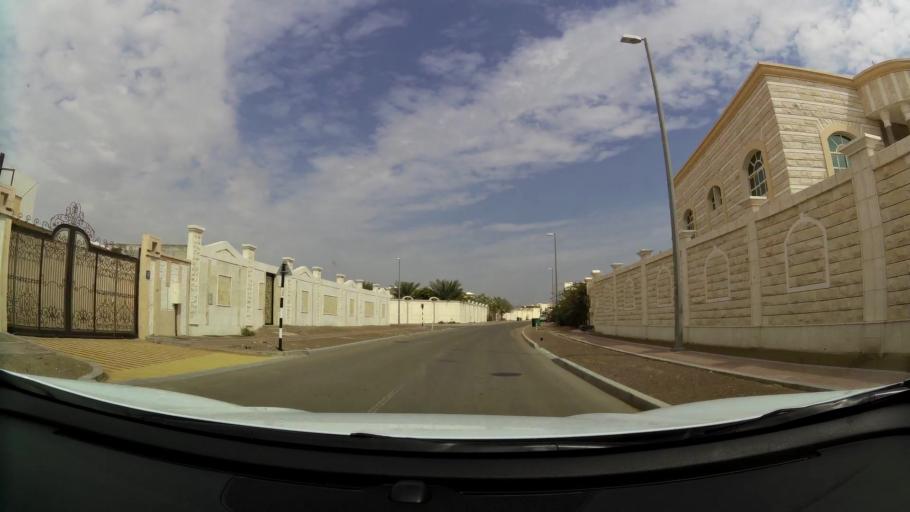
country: AE
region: Abu Dhabi
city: Al Ain
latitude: 24.1858
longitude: 55.8023
